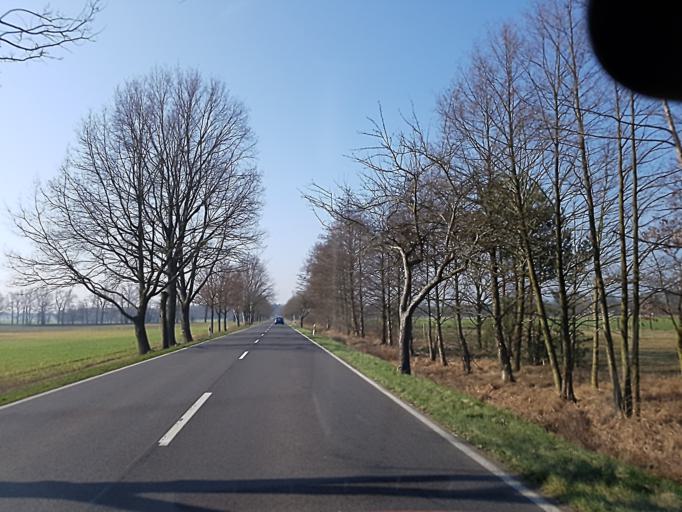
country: DE
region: Brandenburg
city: Tschernitz
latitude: 51.6584
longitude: 14.5901
